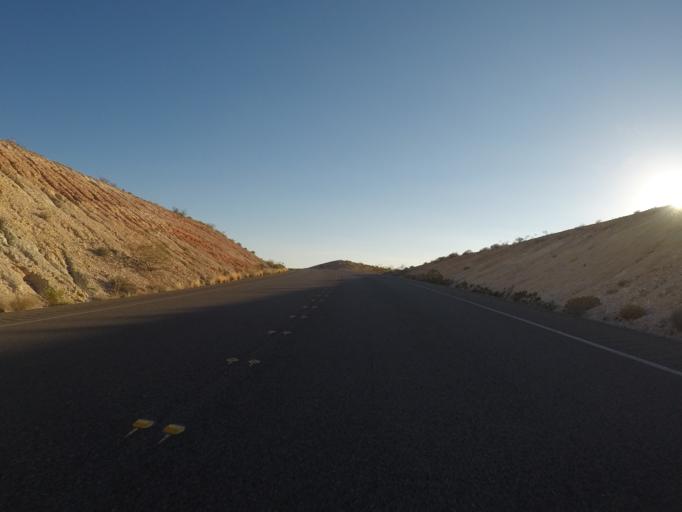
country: US
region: Nevada
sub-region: Clark County
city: Moapa Valley
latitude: 36.3595
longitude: -114.4836
